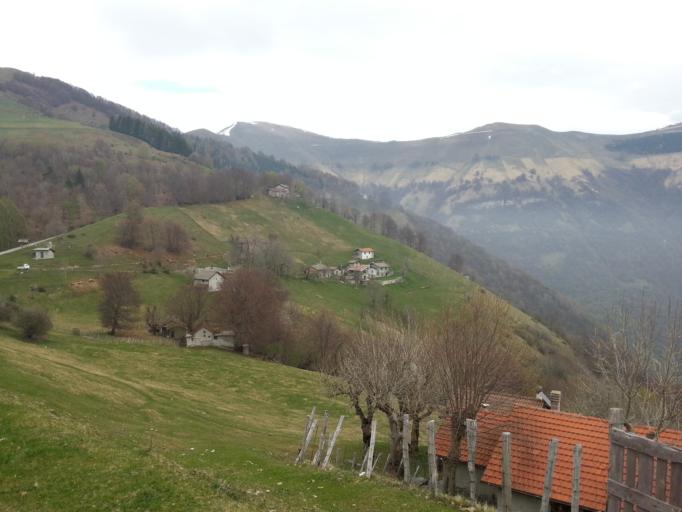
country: IT
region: Lombardy
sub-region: Provincia di Como
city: Sala Comacina
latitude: 45.9880
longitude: 9.1511
